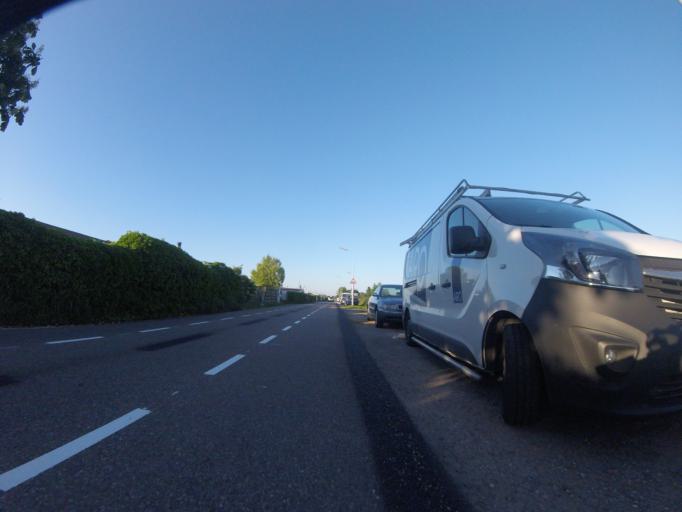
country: NL
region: North Holland
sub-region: Gemeente Haarlem
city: Haarlem
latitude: 52.3483
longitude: 4.6684
